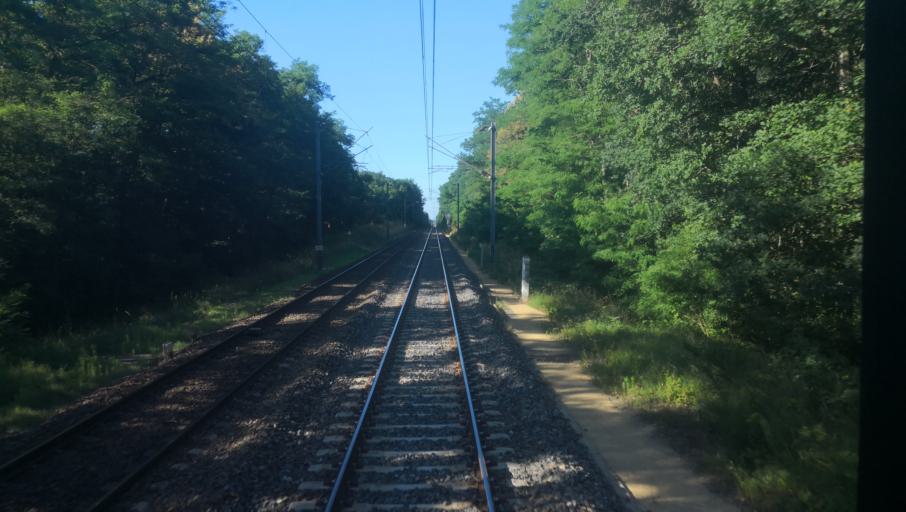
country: FR
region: Centre
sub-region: Departement du Cher
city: Saint-Satur
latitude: 47.3510
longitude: 2.8853
